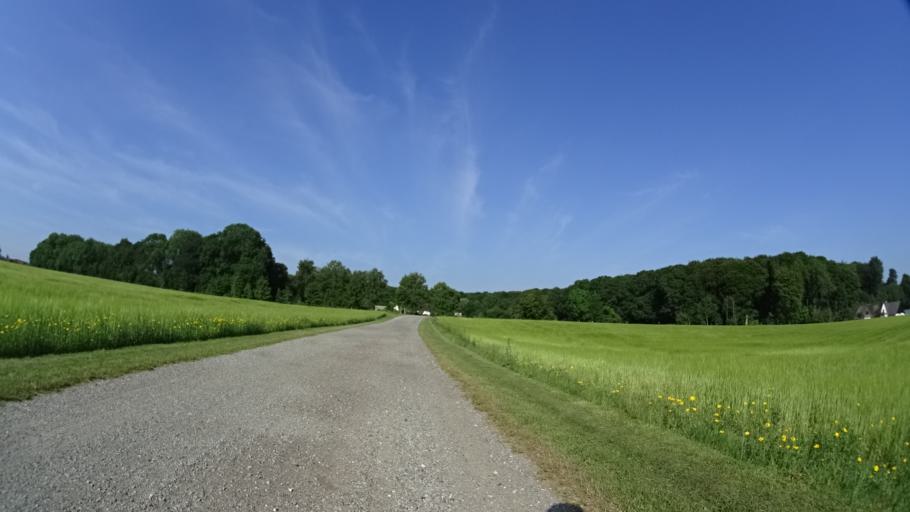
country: DK
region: Central Jutland
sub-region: Arhus Kommune
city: Stavtrup
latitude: 56.1372
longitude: 10.1088
